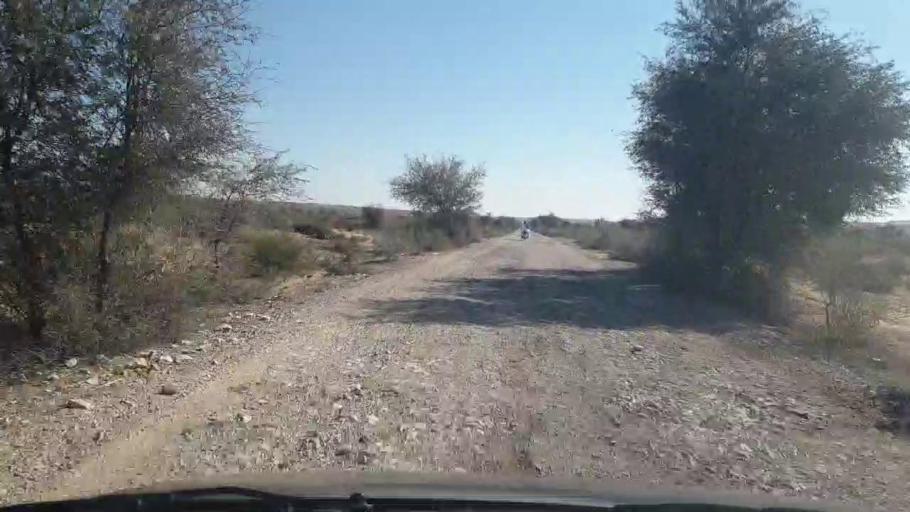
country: PK
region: Sindh
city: Bozdar
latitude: 27.0341
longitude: 68.6992
